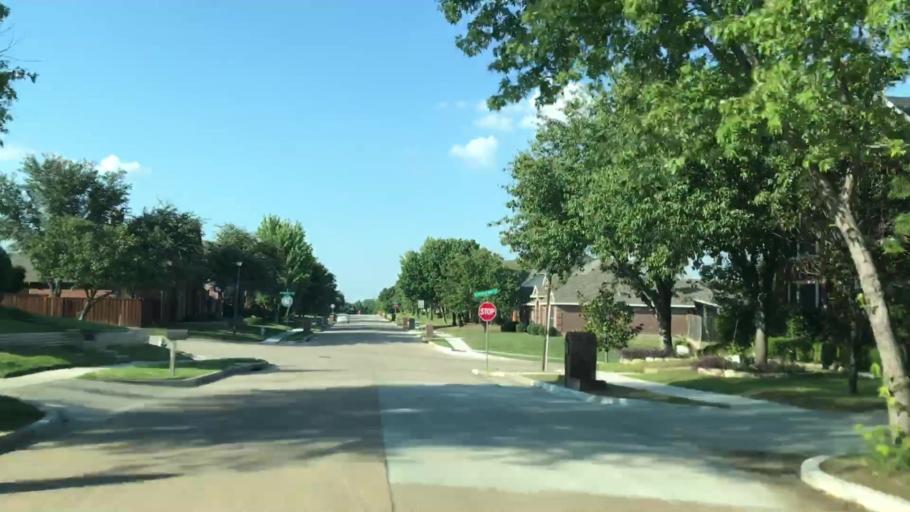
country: US
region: Texas
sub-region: Denton County
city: Lewisville
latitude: 33.0120
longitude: -97.0111
